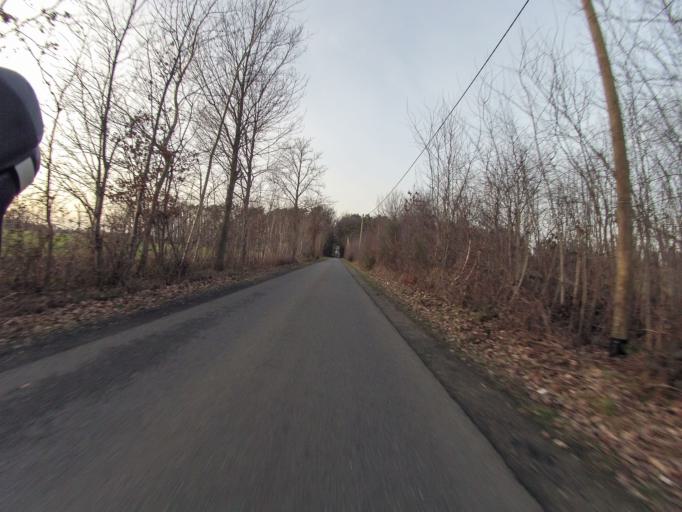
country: DE
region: North Rhine-Westphalia
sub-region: Regierungsbezirk Munster
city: Steinfurt
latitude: 52.1742
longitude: 7.3336
